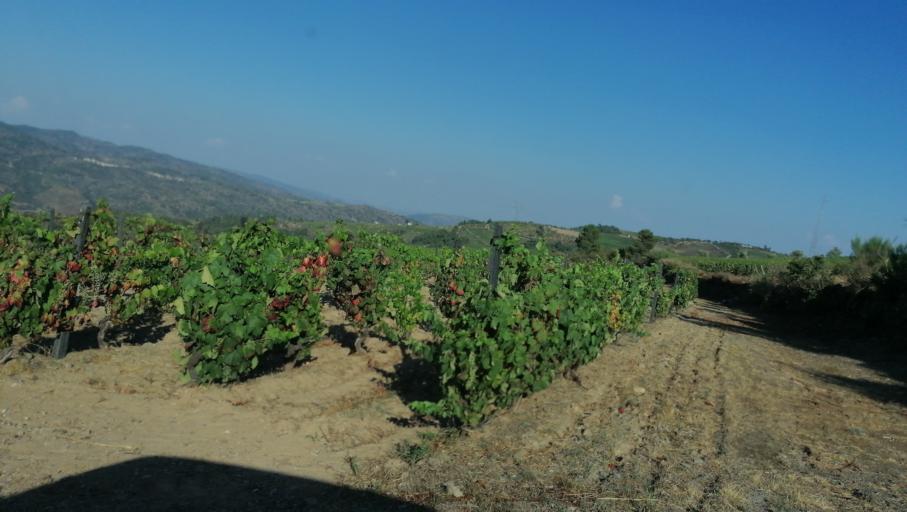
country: PT
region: Viseu
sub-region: Sao Joao da Pesqueira
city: Sao Joao da Pesqueira
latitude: 41.1663
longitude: -7.4089
